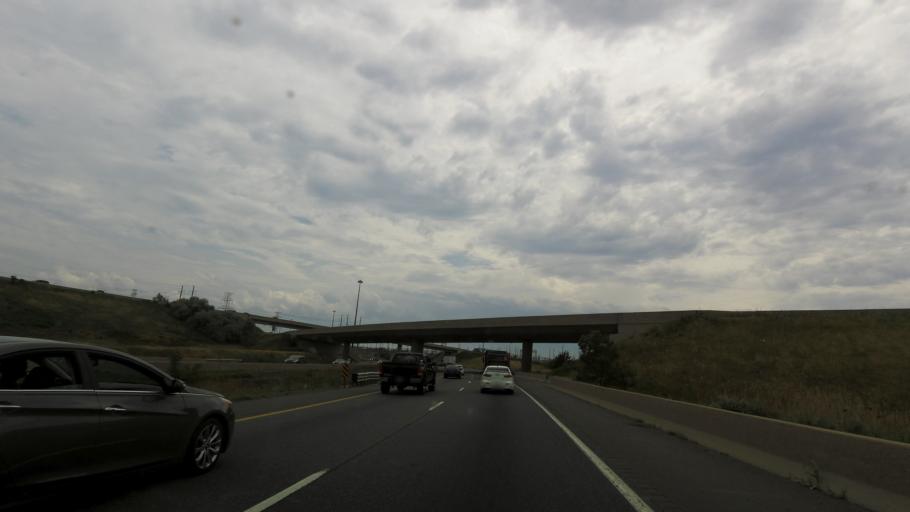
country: CA
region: Ontario
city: Burlington
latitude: 43.3386
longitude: -79.8281
